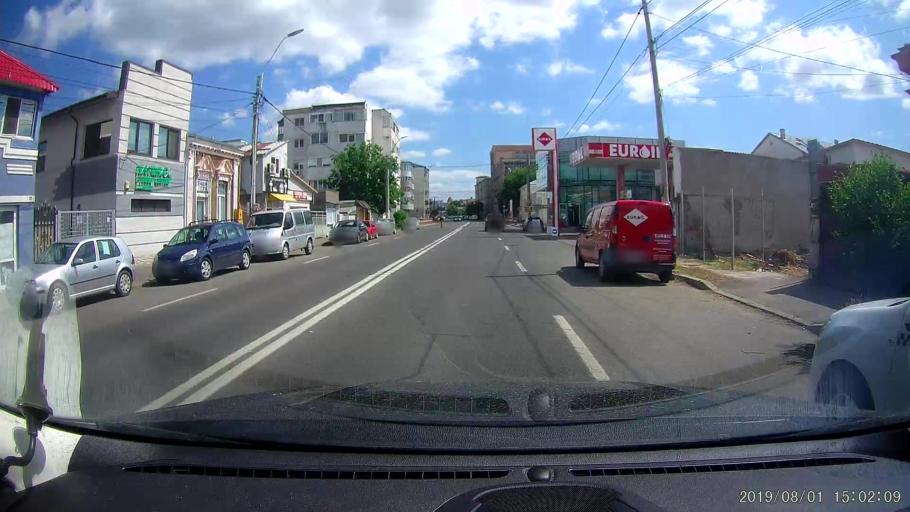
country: RO
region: Braila
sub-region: Municipiul Braila
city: Braila
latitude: 45.2674
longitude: 27.9611
